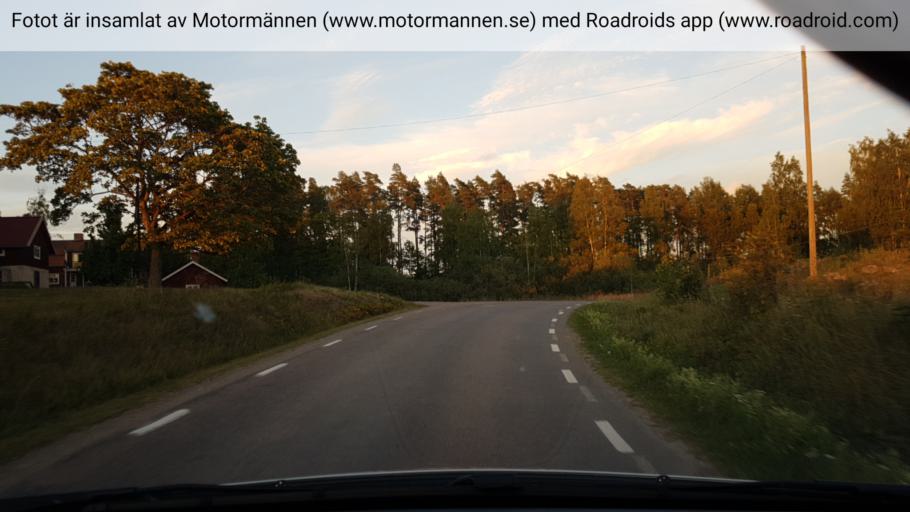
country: SE
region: Vaestmanland
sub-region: Hallstahammars Kommun
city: Kolback
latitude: 59.5614
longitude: 16.2110
